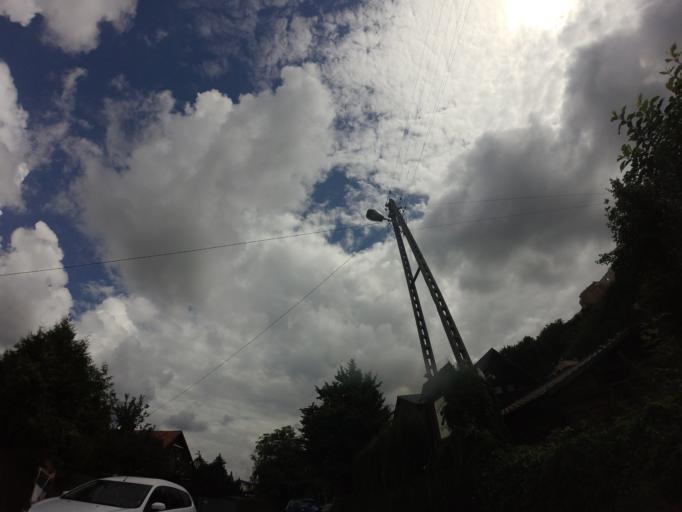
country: PL
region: Lublin Voivodeship
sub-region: Powiat pulawski
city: Kazimierz Dolny
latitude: 51.3239
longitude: 21.9484
